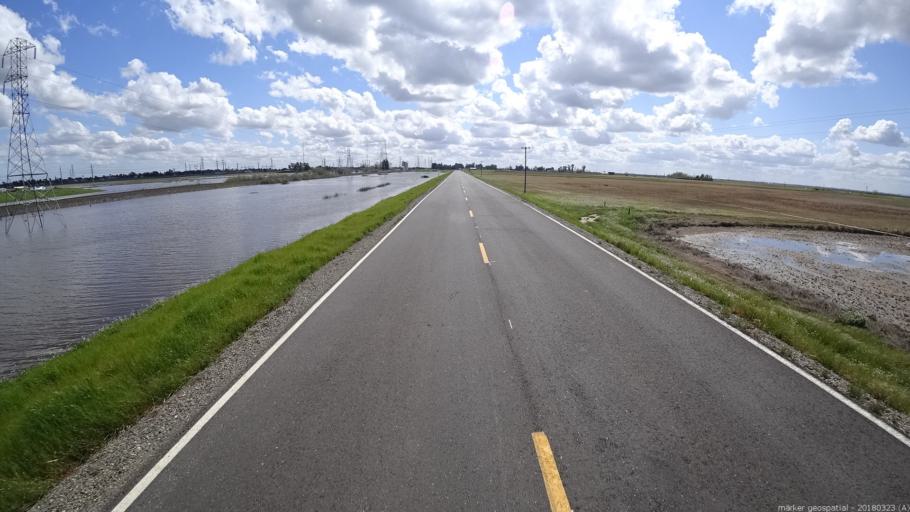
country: US
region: California
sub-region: Sacramento County
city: Elverta
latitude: 38.7222
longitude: -121.4881
